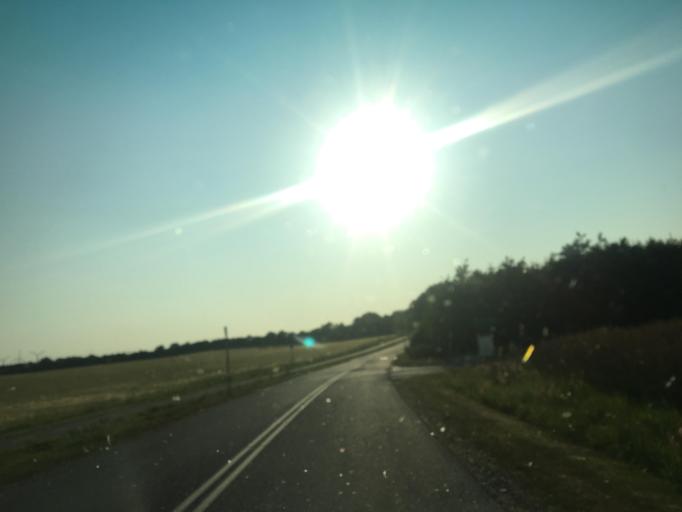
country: DK
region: North Denmark
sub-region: Thisted Kommune
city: Hurup
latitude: 56.8151
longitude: 8.3914
